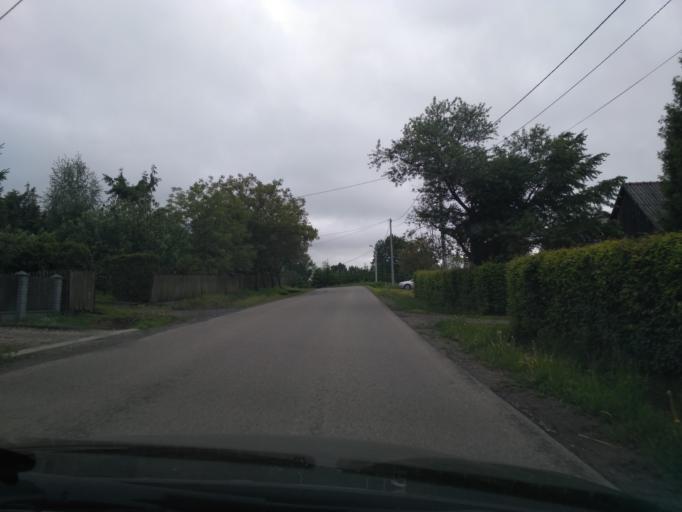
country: PL
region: Subcarpathian Voivodeship
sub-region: Powiat jasielski
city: Jaslo
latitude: 49.8021
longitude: 21.5318
